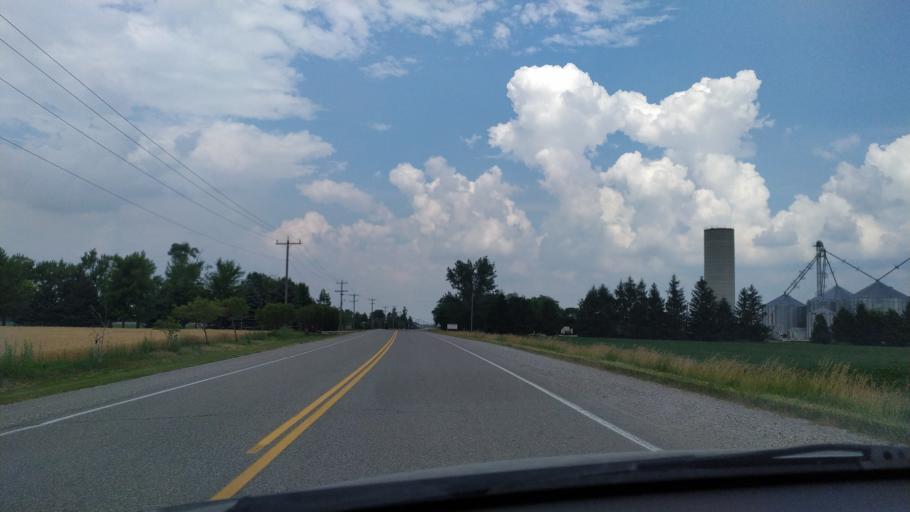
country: CA
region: Ontario
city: London
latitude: 43.1595
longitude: -81.1610
